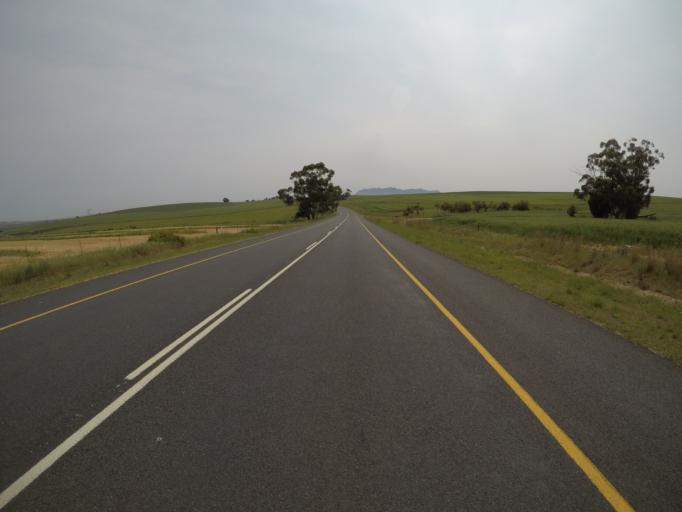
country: ZA
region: Western Cape
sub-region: West Coast District Municipality
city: Malmesbury
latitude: -33.5160
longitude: 18.8460
